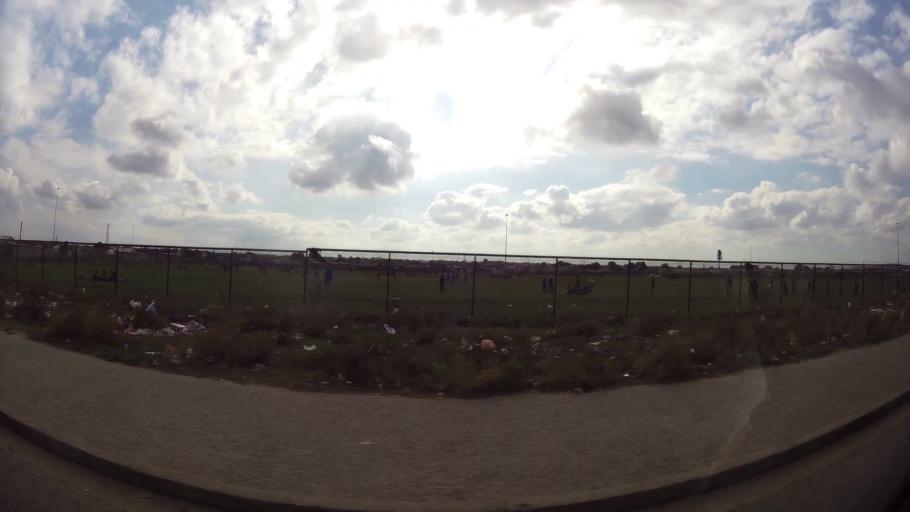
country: ZA
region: Eastern Cape
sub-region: Nelson Mandela Bay Metropolitan Municipality
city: Port Elizabeth
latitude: -33.8068
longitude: 25.5882
